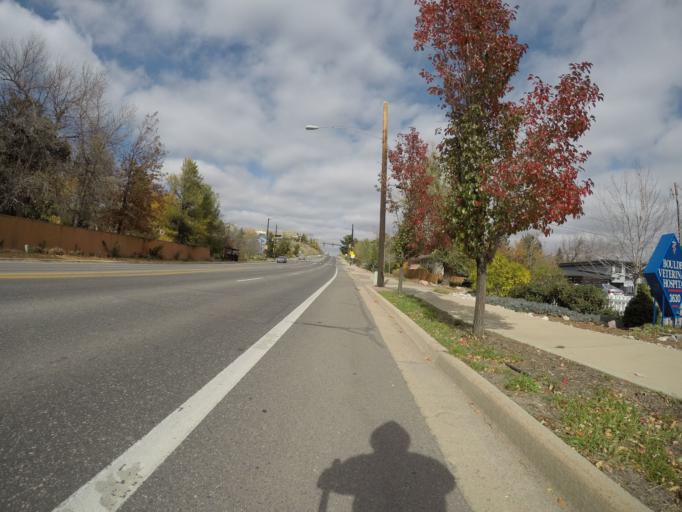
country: US
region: Colorado
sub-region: Boulder County
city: Boulder
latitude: 40.0400
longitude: -105.2820
